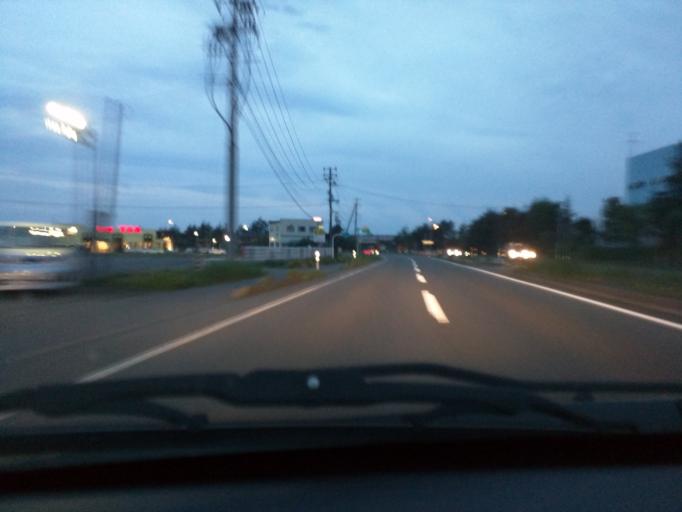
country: JP
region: Niigata
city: Kashiwazaki
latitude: 37.3600
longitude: 138.5913
